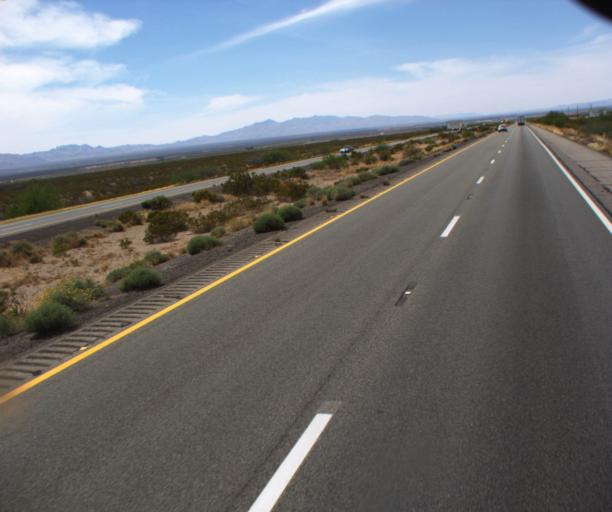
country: US
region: New Mexico
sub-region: Hidalgo County
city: Lordsburg
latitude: 32.2462
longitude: -109.1292
